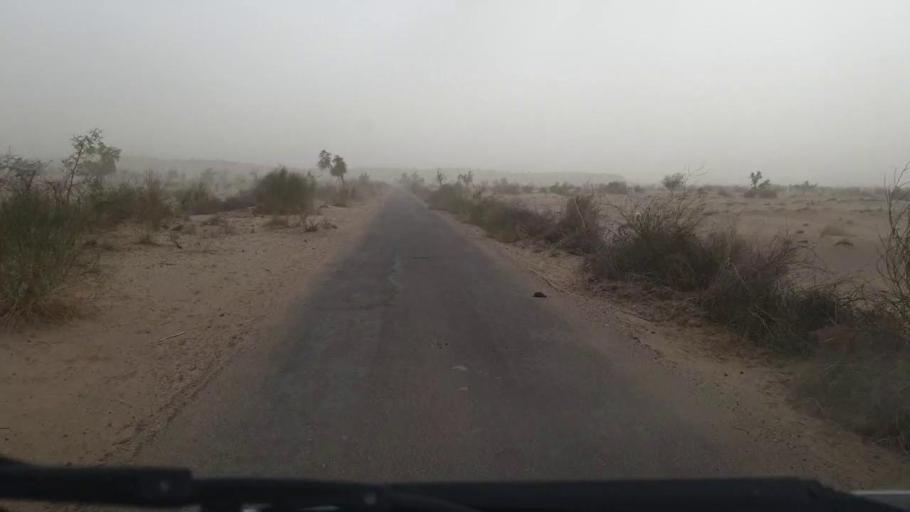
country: PK
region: Sindh
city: Islamkot
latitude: 25.0685
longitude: 70.5591
